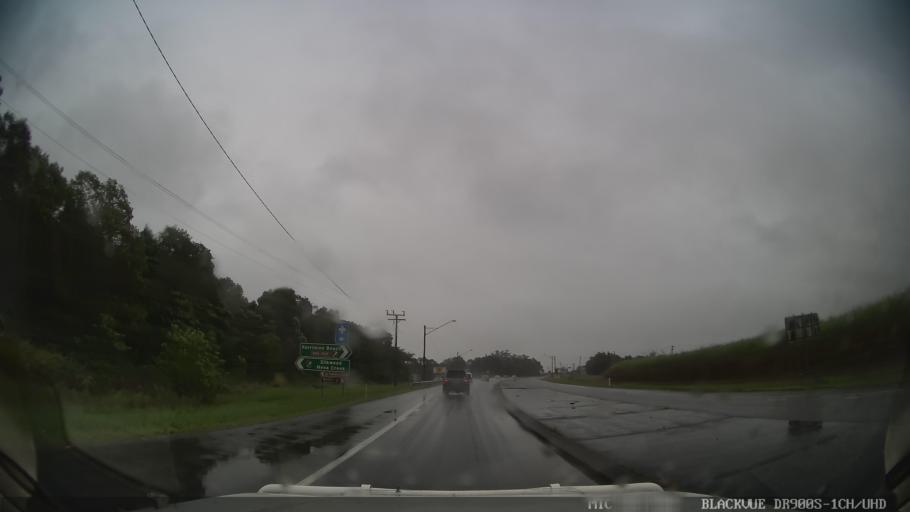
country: AU
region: Queensland
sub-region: Cassowary Coast
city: Innisfail
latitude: -17.7501
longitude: 146.0277
